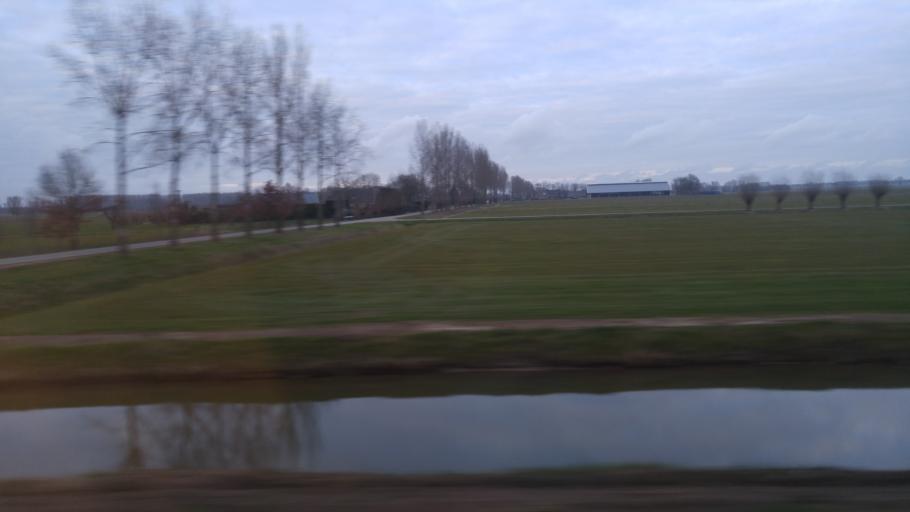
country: NL
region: Gelderland
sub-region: Gemeente Culemborg
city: Culemborg
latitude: 51.9154
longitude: 5.2520
